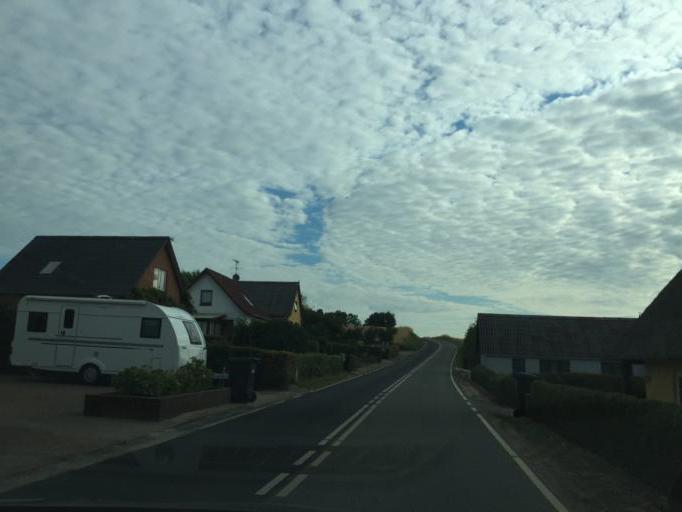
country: DK
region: South Denmark
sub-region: Assens Kommune
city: Assens
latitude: 55.2869
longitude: 9.9781
